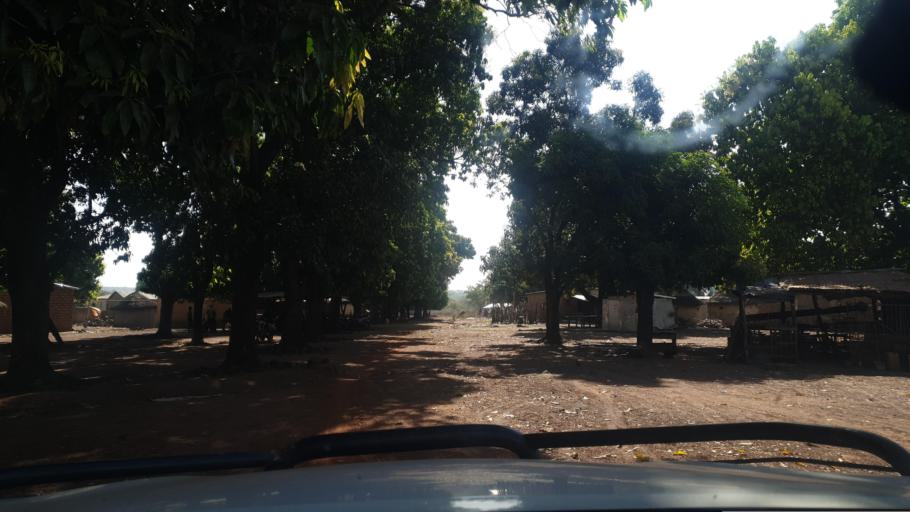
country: GN
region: Kankan
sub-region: Mandiana Prefecture
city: Mandiana
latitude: 10.4892
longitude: -8.0976
